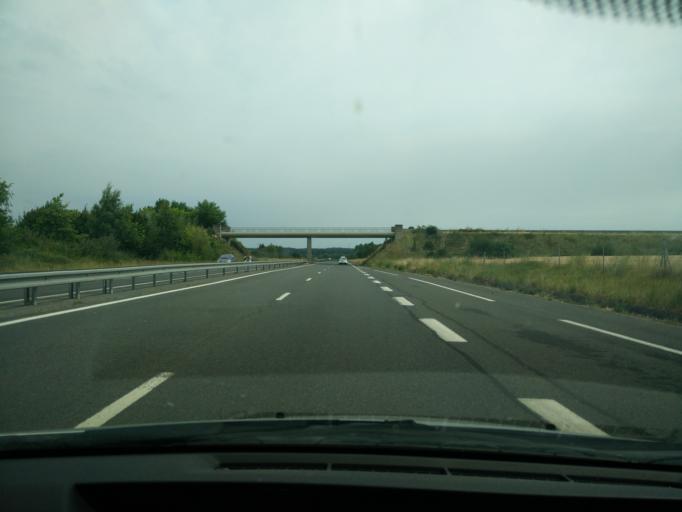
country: FR
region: Pays de la Loire
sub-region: Departement de Maine-et-Loire
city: Doue-la-Fontaine
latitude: 47.1983
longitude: -0.3168
